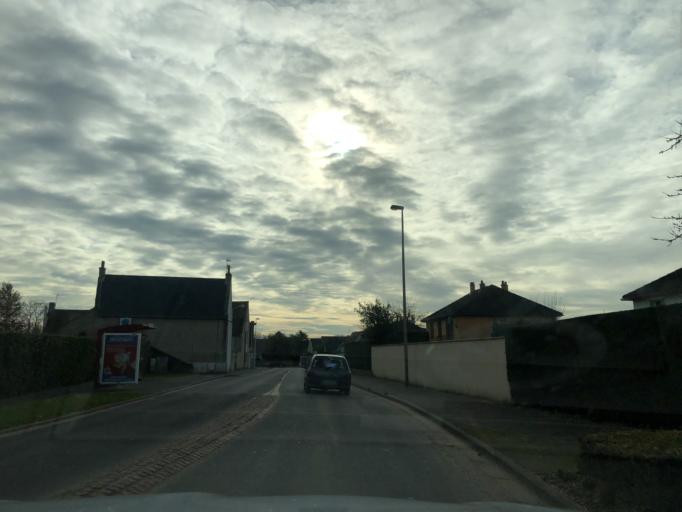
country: FR
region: Lower Normandy
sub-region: Departement du Calvados
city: Beuville
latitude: 49.2462
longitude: -0.3304
